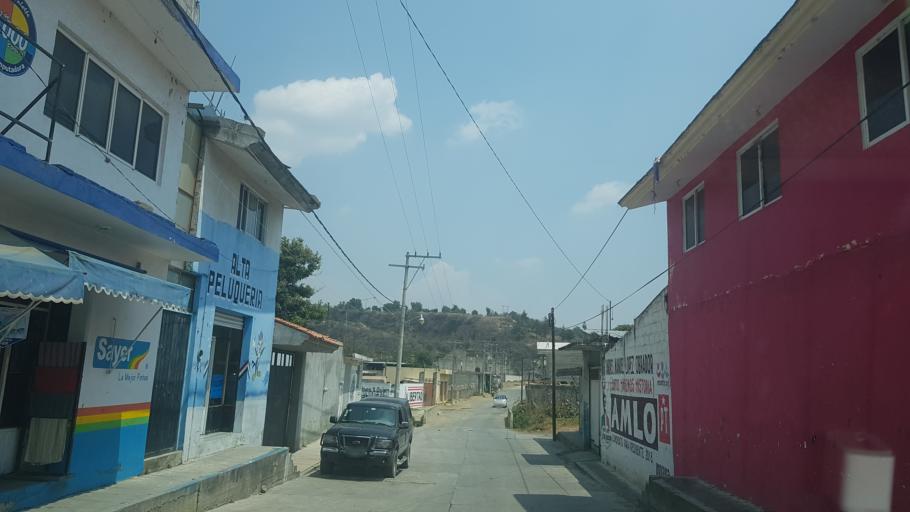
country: MX
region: Puebla
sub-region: San Nicolas de los Ranchos
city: San Pedro Yancuitlalpan
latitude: 19.0769
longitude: -98.4841
